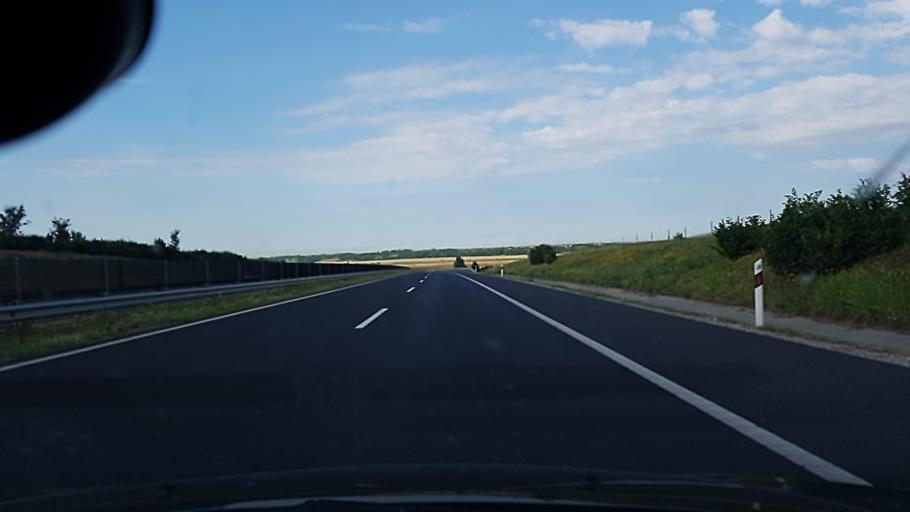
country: HU
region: Fejer
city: Rackeresztur
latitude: 47.2392
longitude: 18.8266
